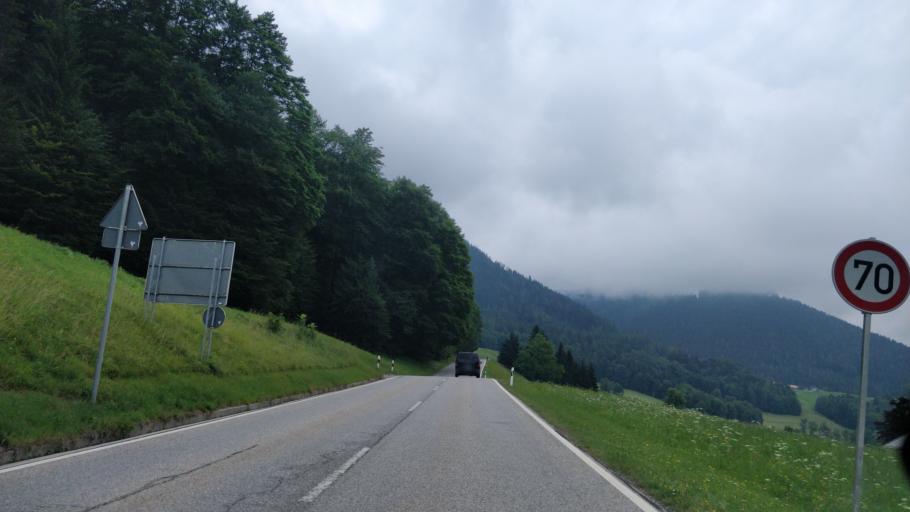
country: AT
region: Salzburg
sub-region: Politischer Bezirk Hallein
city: Hallein
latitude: 47.6583
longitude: 13.0756
